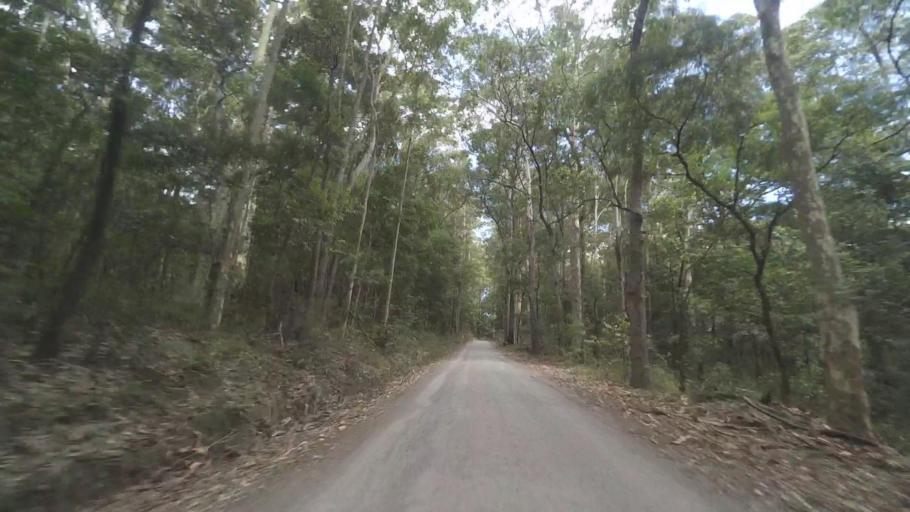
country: AU
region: New South Wales
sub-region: Shoalhaven Shire
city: Milton
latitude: -35.4407
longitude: 150.3139
